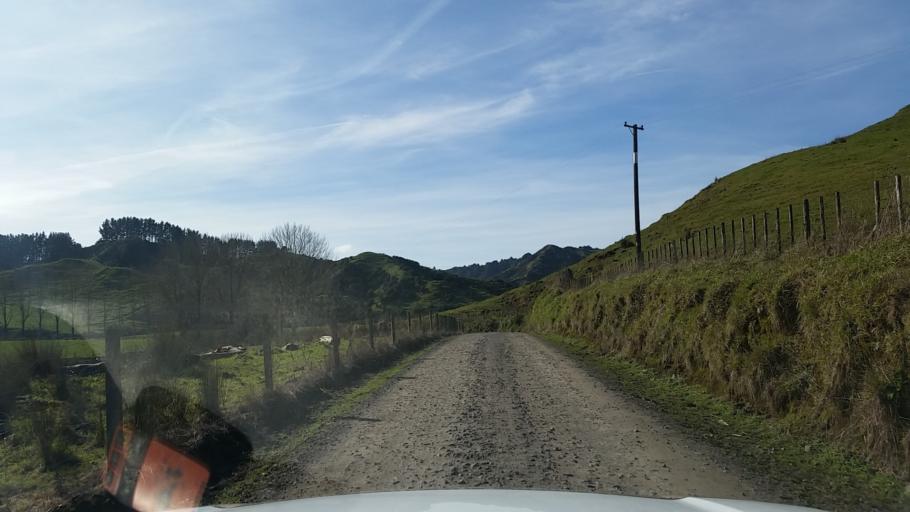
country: NZ
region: Taranaki
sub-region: South Taranaki District
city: Eltham
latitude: -39.3560
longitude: 174.5119
